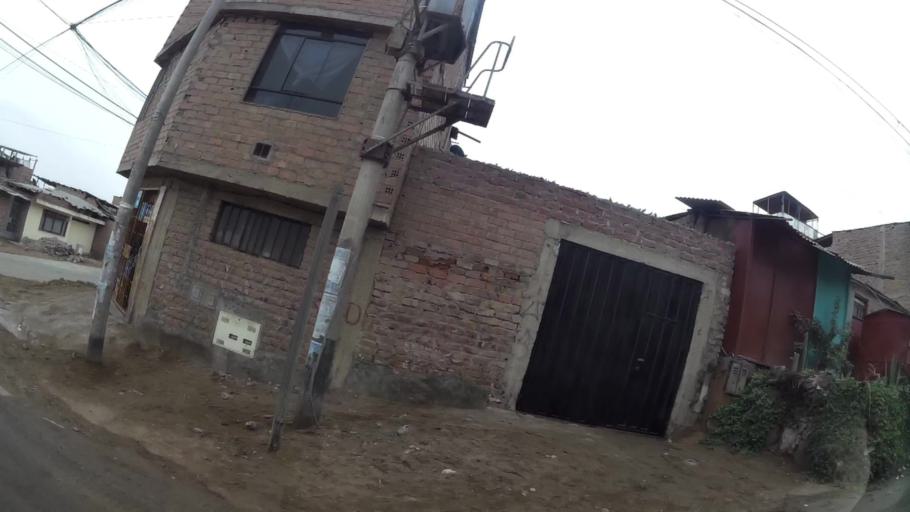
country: PE
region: Lima
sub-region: Lima
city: Surco
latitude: -12.1740
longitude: -76.9587
